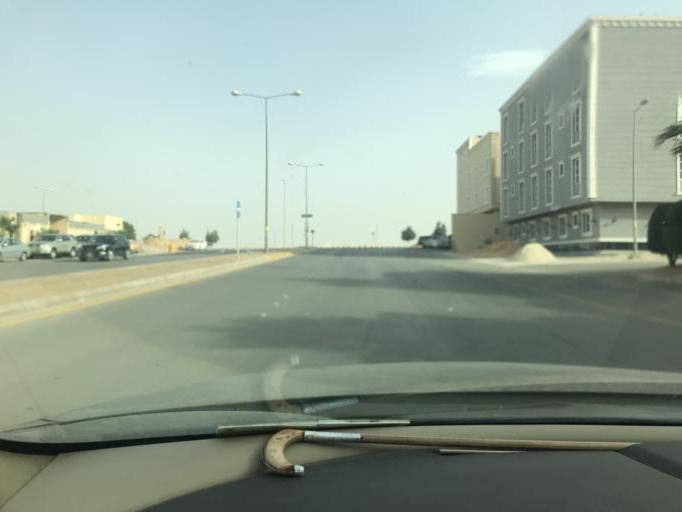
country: SA
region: Ar Riyad
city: Riyadh
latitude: 24.7818
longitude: 46.7155
